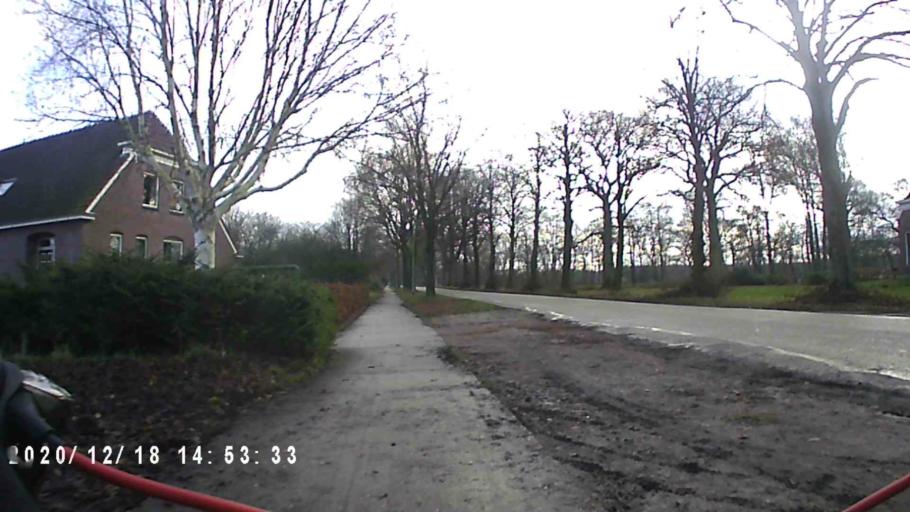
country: NL
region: Groningen
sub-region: Gemeente Haren
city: Haren
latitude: 53.1900
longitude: 6.6802
